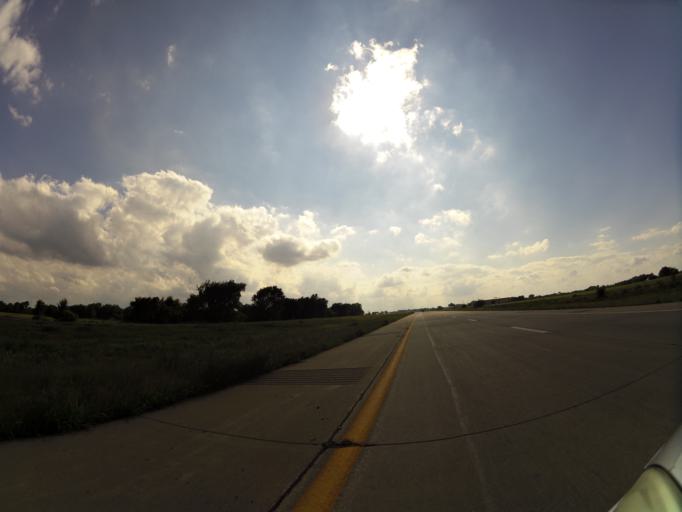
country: US
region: Kansas
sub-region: Reno County
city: Haven
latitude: 37.8766
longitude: -97.6566
